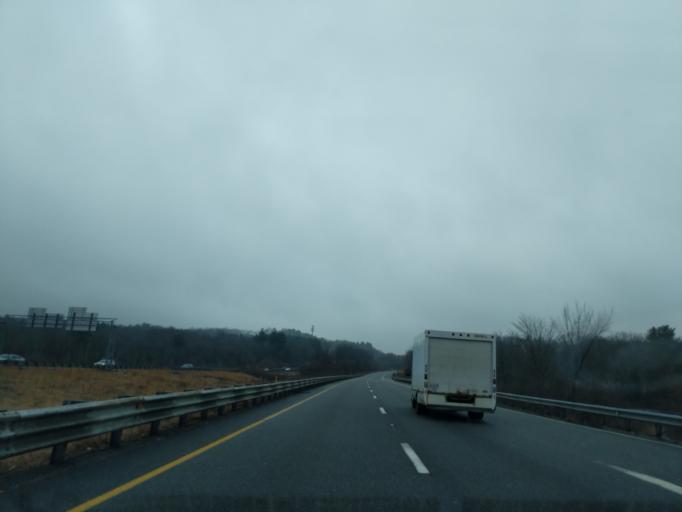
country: US
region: Massachusetts
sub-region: Worcester County
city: Oxford
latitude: 42.1119
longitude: -71.8553
